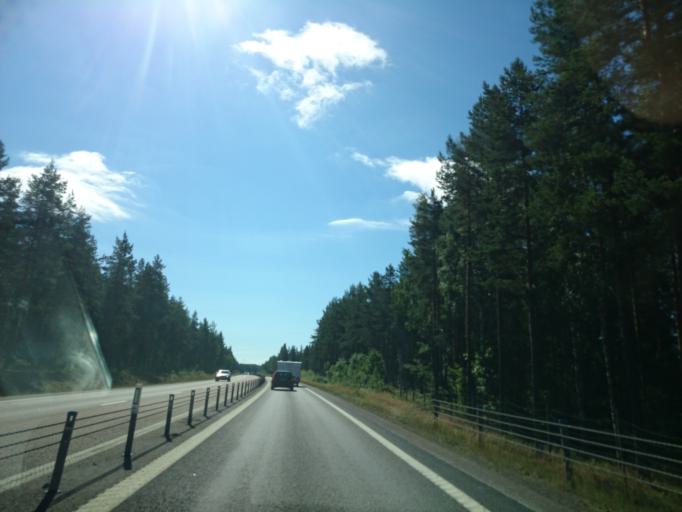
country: SE
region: Gaevleborg
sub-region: Gavle Kommun
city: Norrsundet
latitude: 60.9958
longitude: 16.9964
